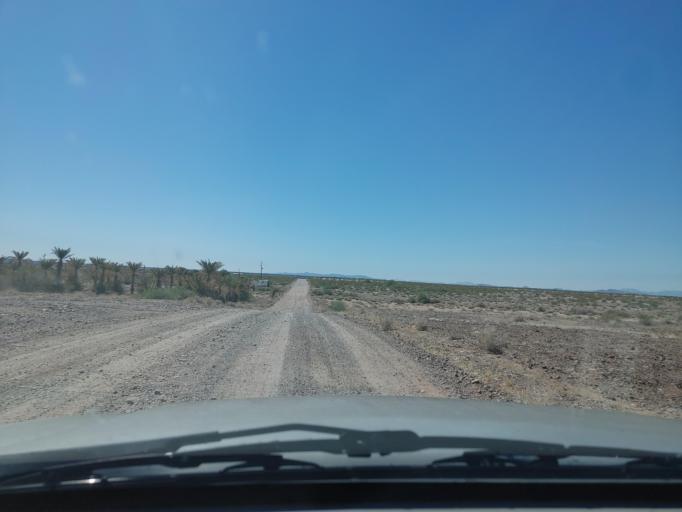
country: US
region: Arizona
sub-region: Maricopa County
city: Gila Bend
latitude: 32.9911
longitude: -113.3404
